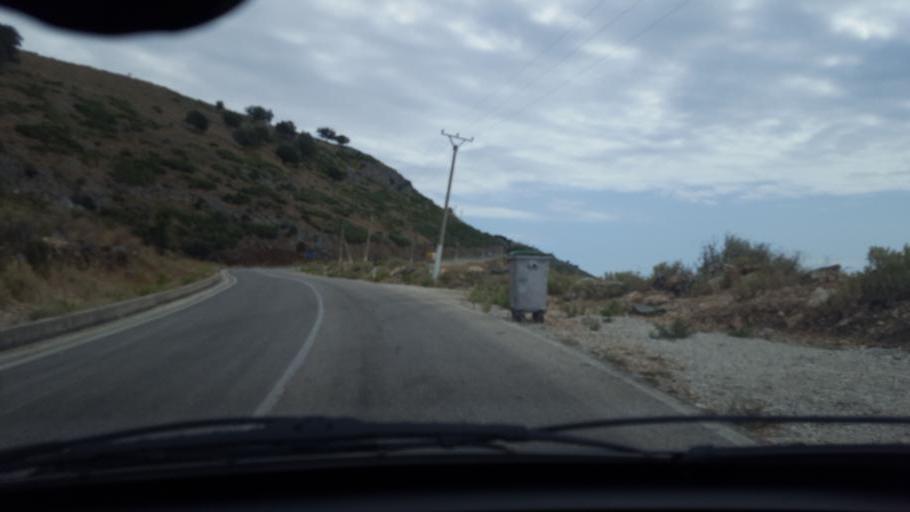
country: AL
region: Vlore
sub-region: Rrethi i Sarandes
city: Lukove
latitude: 40.0473
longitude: 19.8706
